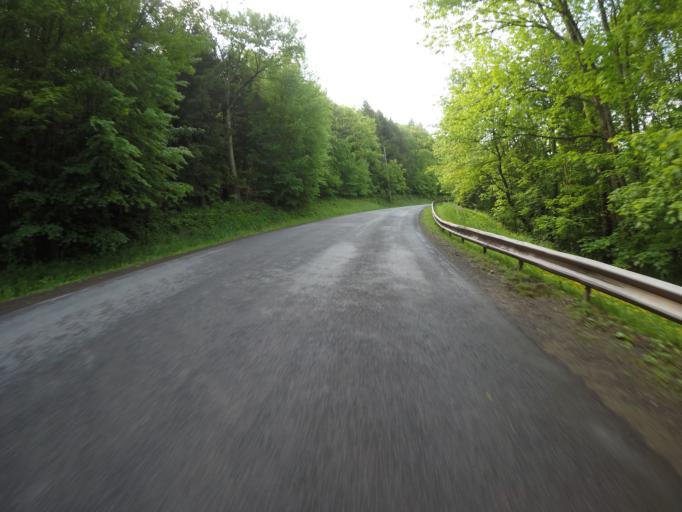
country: US
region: New York
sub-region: Delaware County
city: Stamford
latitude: 42.1775
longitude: -74.6673
